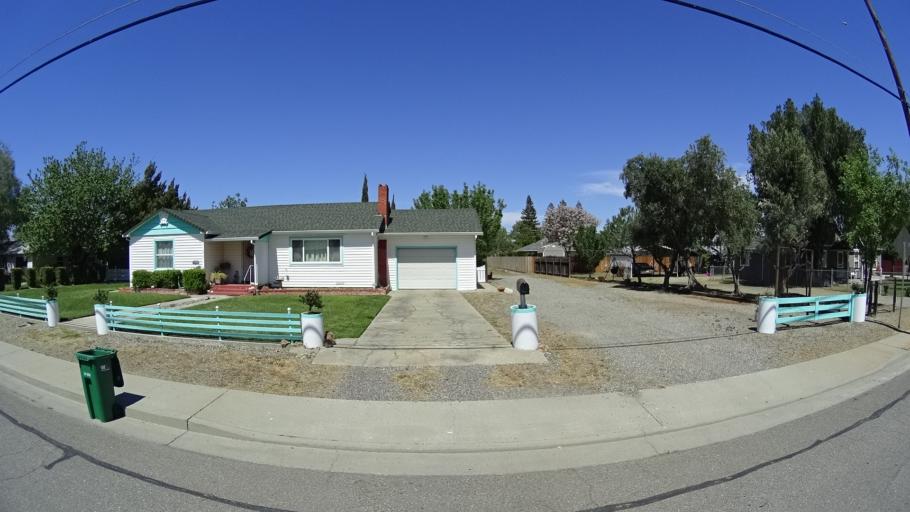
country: US
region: California
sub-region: Glenn County
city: Orland
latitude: 39.7436
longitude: -122.1809
